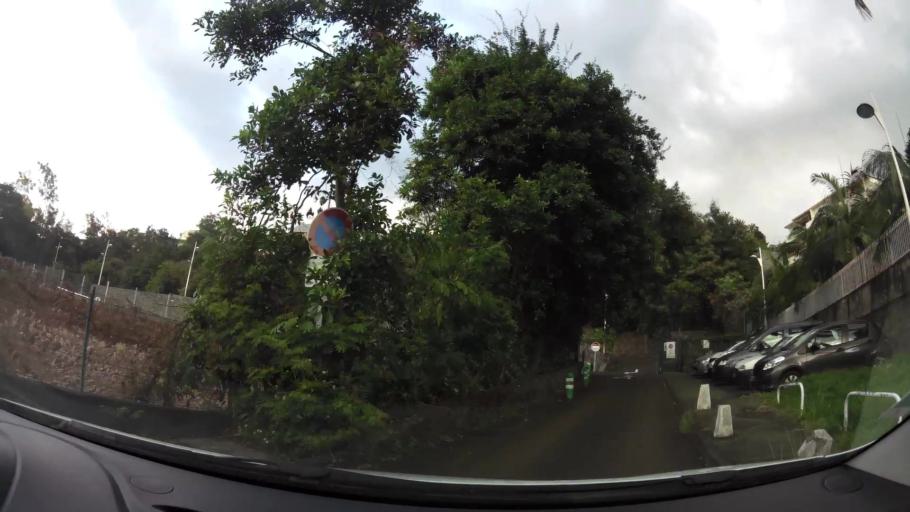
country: RE
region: Reunion
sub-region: Reunion
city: Saint-Denis
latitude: -20.8941
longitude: 55.4424
